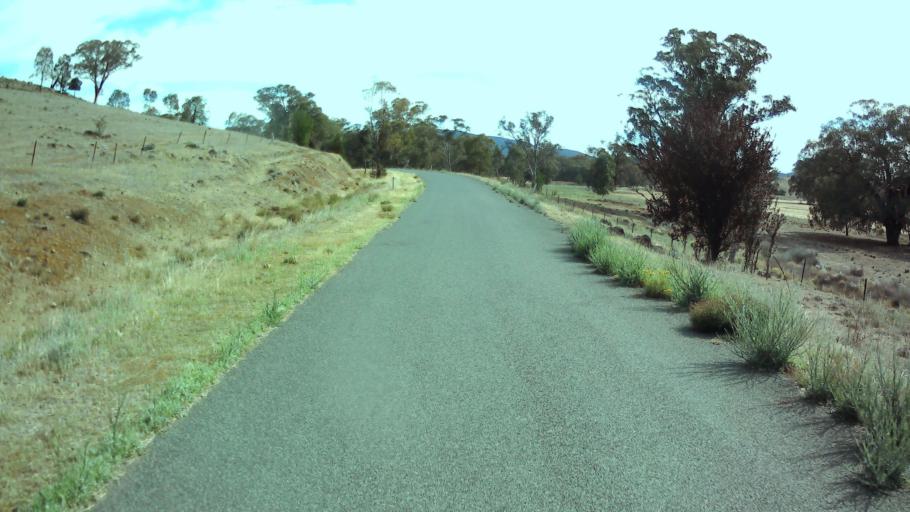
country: AU
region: New South Wales
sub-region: Weddin
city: Grenfell
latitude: -33.8183
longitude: 148.2910
